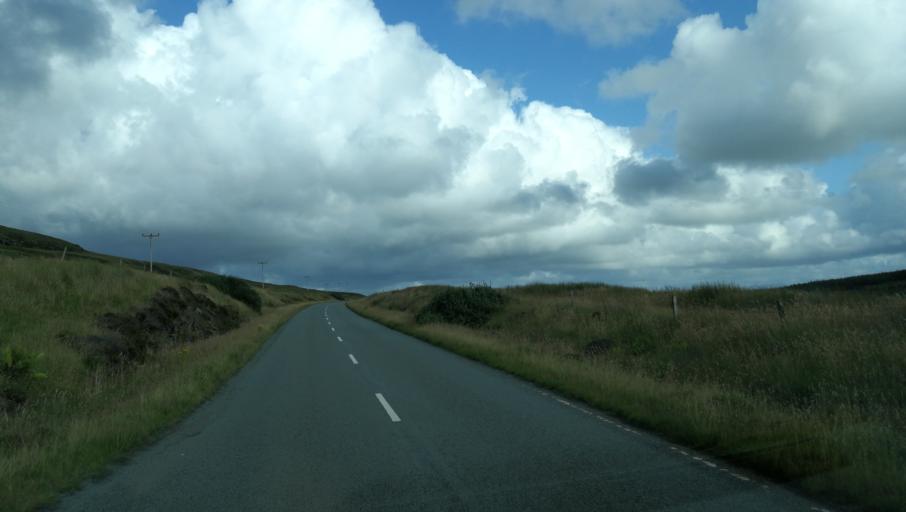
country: GB
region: Scotland
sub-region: Highland
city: Isle of Skye
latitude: 57.4683
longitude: -6.5208
